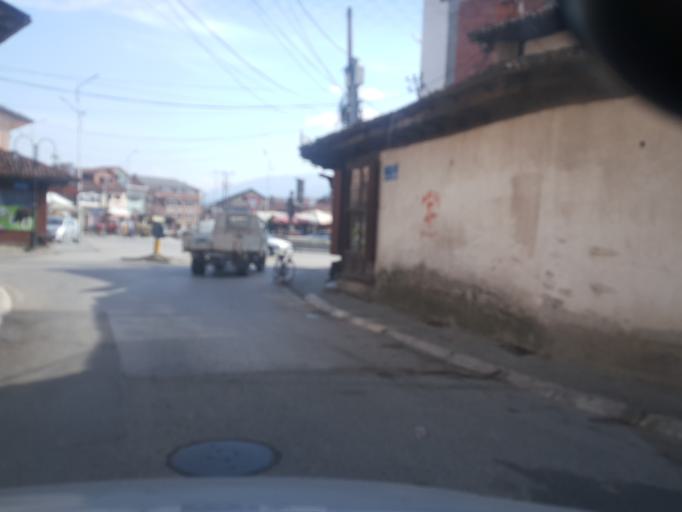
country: XK
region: Gjakova
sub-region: Komuna e Gjakoves
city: Gjakove
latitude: 42.3759
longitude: 20.4254
